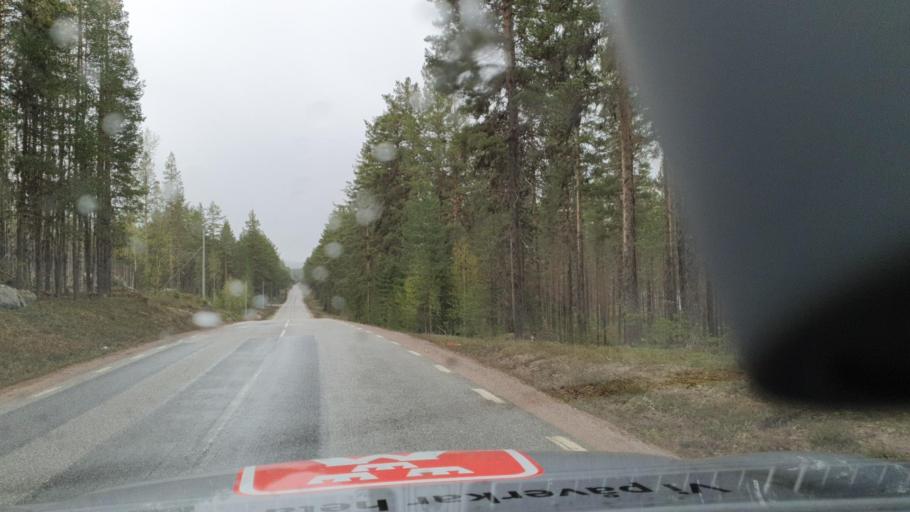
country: SE
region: Vaesternorrland
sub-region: Solleftea Kommun
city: As
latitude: 63.6932
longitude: 17.0249
